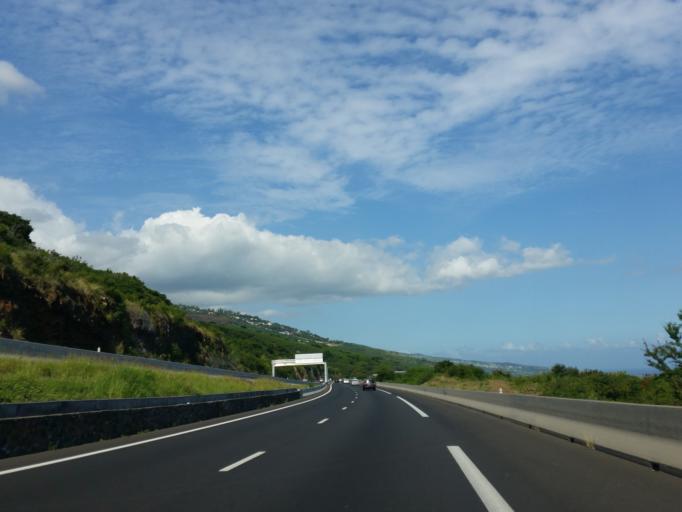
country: RE
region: Reunion
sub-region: Reunion
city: Trois-Bassins
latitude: -21.1158
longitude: 55.2765
